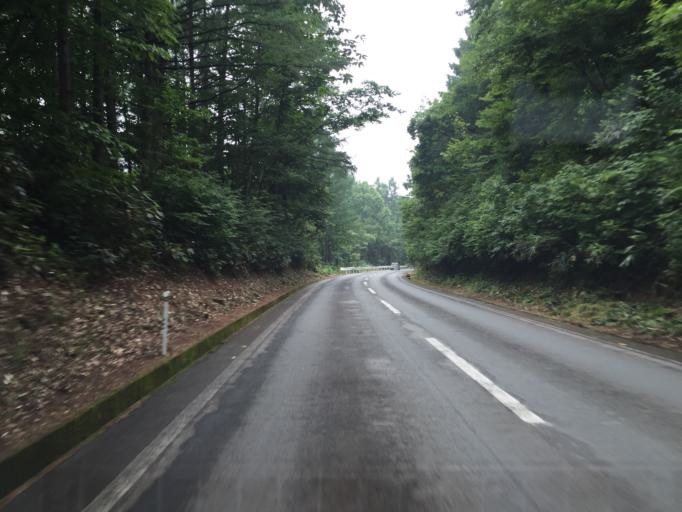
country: JP
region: Fukushima
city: Inawashiro
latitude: 37.6751
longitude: 140.1366
